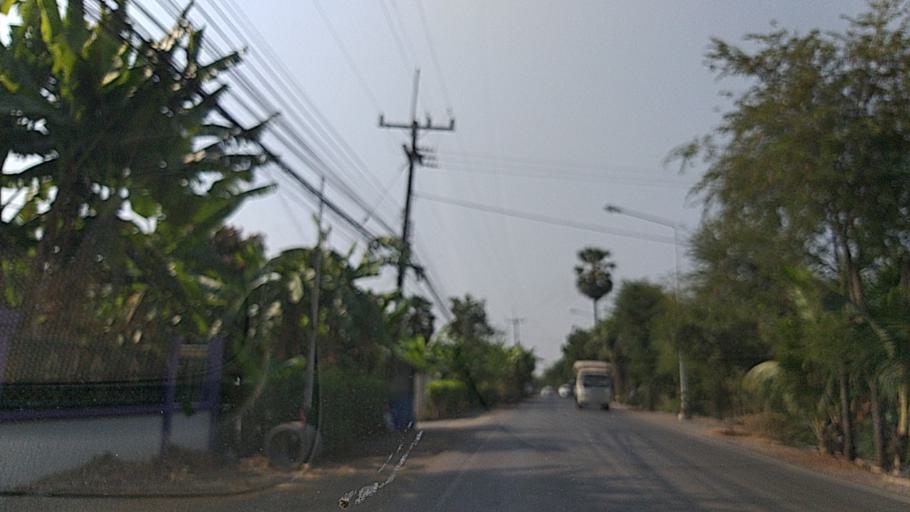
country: TH
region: Pathum Thani
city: Lam Luk Ka
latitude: 13.9493
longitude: 100.7059
